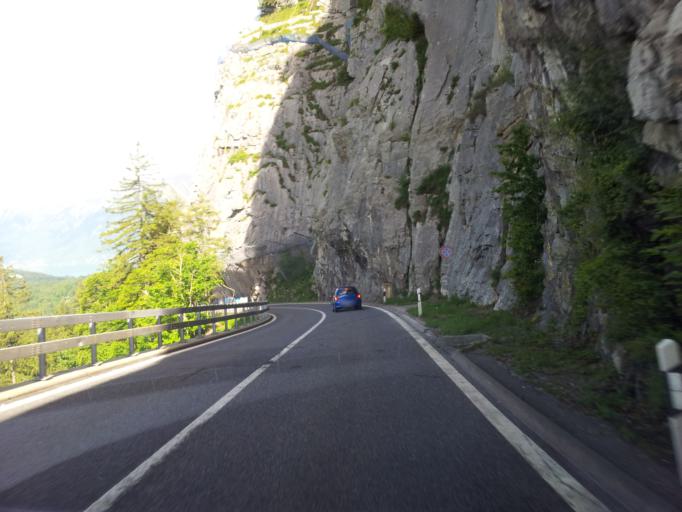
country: CH
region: Obwalden
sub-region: Obwalden
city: Lungern
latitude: 46.7494
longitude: 8.1147
